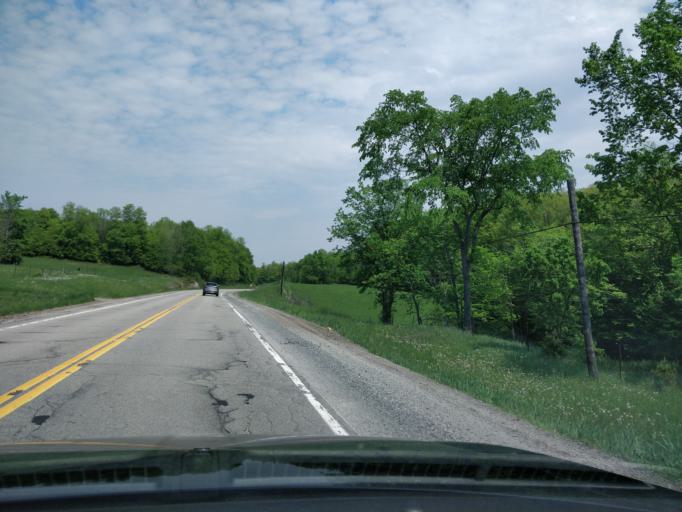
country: CA
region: Ontario
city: Perth
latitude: 44.7622
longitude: -76.3784
